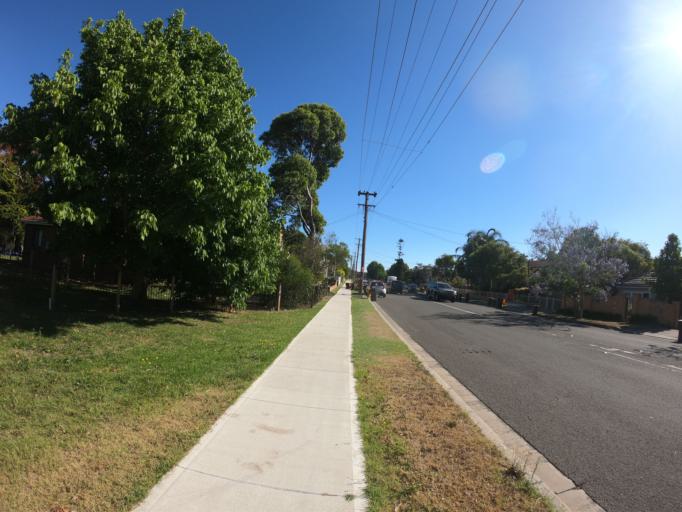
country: AU
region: New South Wales
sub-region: Wollongong
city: Fairy Meadow
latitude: -34.3981
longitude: 150.8960
